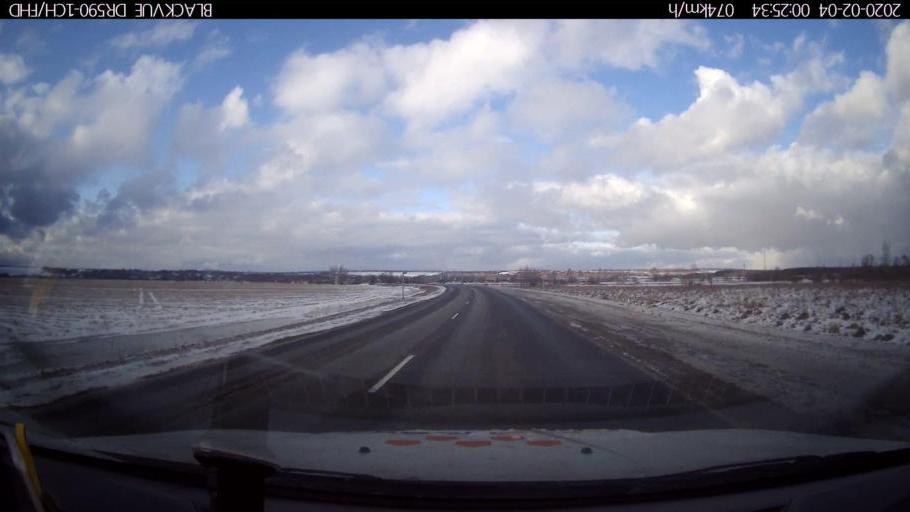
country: RU
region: Nizjnij Novgorod
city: Kstovo
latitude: 56.0071
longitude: 44.2092
